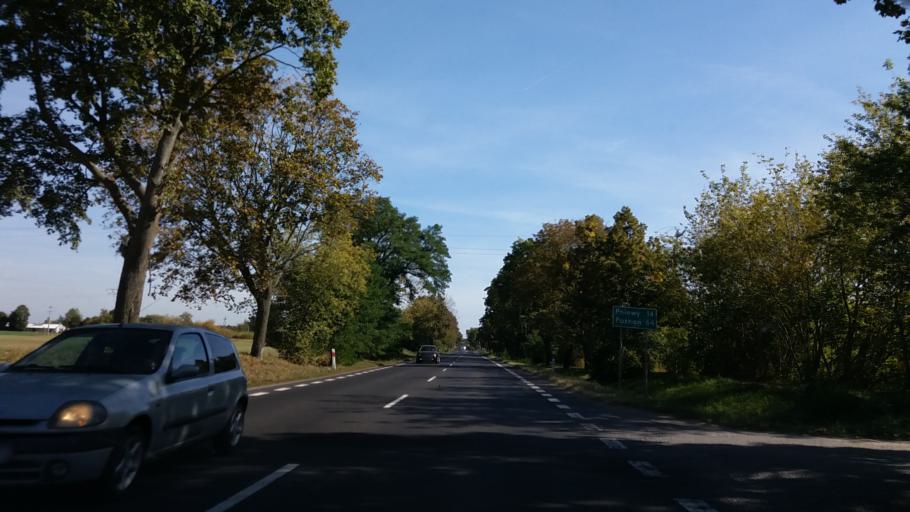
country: PL
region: Greater Poland Voivodeship
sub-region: Powiat miedzychodzki
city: Kwilcz
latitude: 52.5566
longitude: 16.0721
